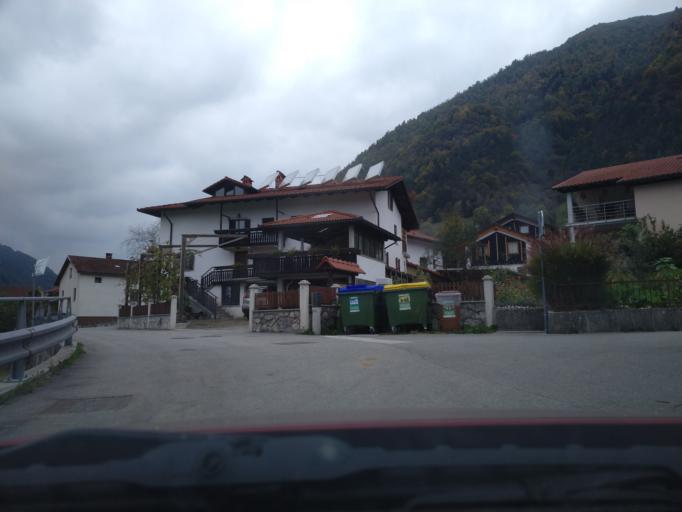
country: SI
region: Tolmin
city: Tolmin
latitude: 46.1943
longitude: 13.7292
